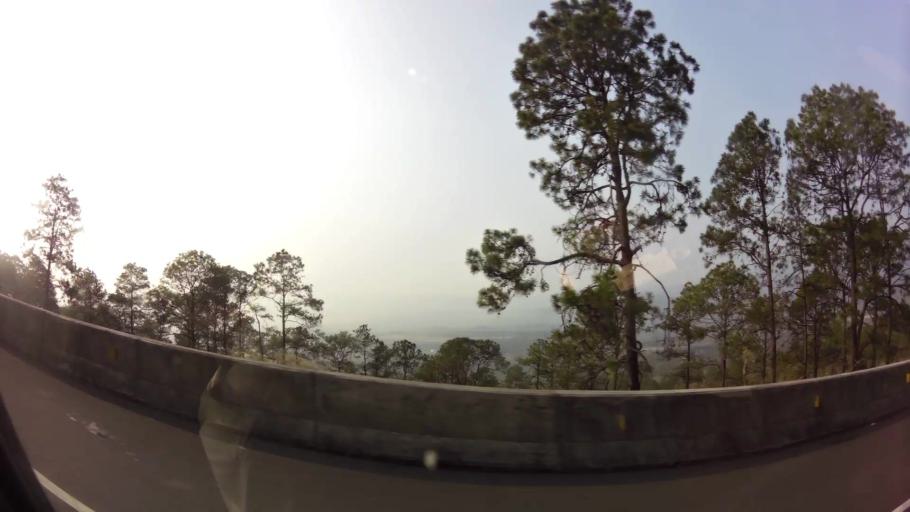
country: HN
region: Francisco Morazan
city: Zambrano
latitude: 14.2433
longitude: -87.3819
